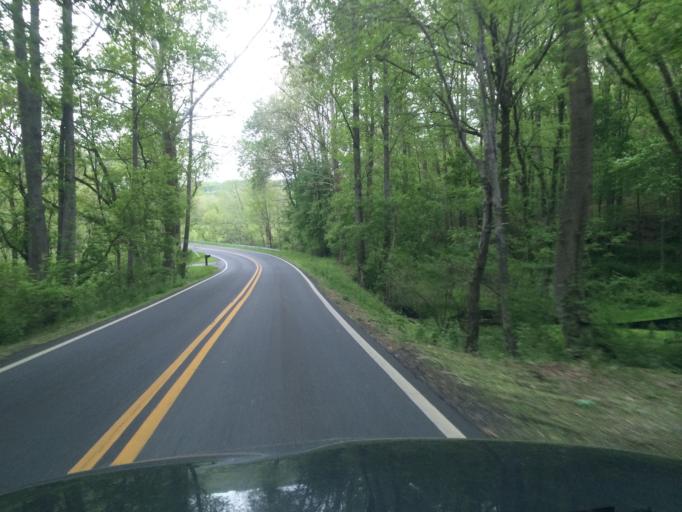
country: US
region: Maryland
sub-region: Carroll County
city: Eldersburg
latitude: 39.4256
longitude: -76.9614
